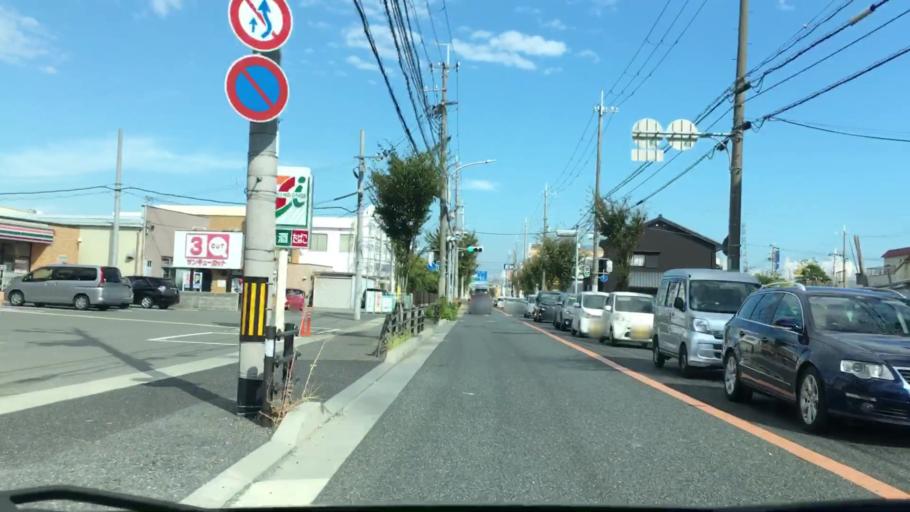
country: JP
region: Hyogo
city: Akashi
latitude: 34.6689
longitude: 134.9774
